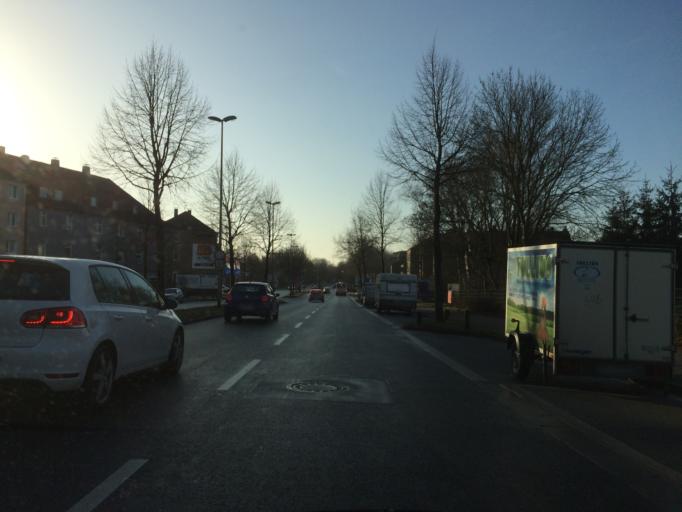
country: DE
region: North Rhine-Westphalia
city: Bochum-Hordel
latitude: 51.5265
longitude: 7.1882
